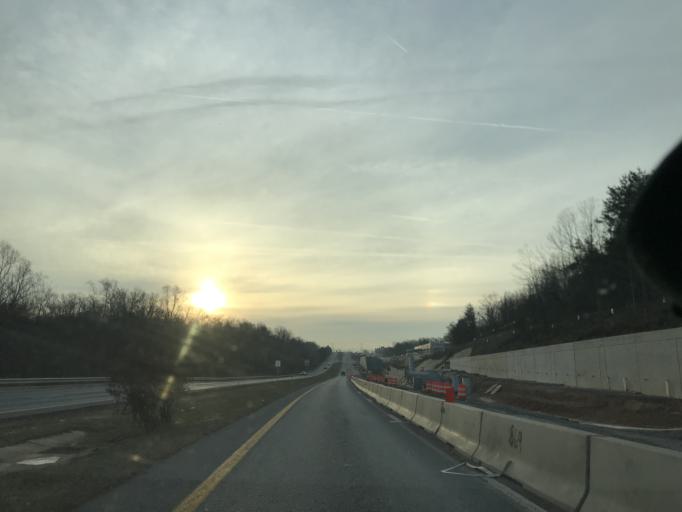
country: US
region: Maryland
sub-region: Prince George's County
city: Woodlawn
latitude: 38.9590
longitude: -76.8930
